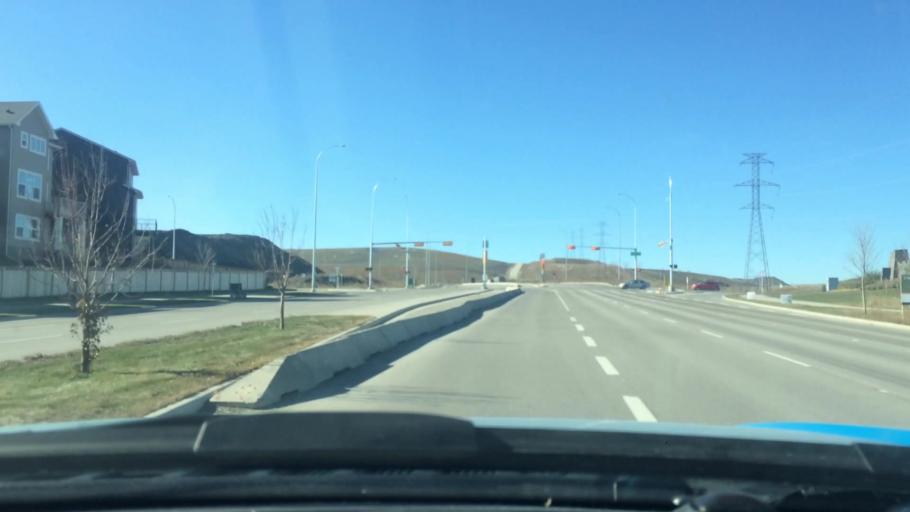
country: CA
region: Alberta
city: Calgary
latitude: 51.1681
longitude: -114.1589
